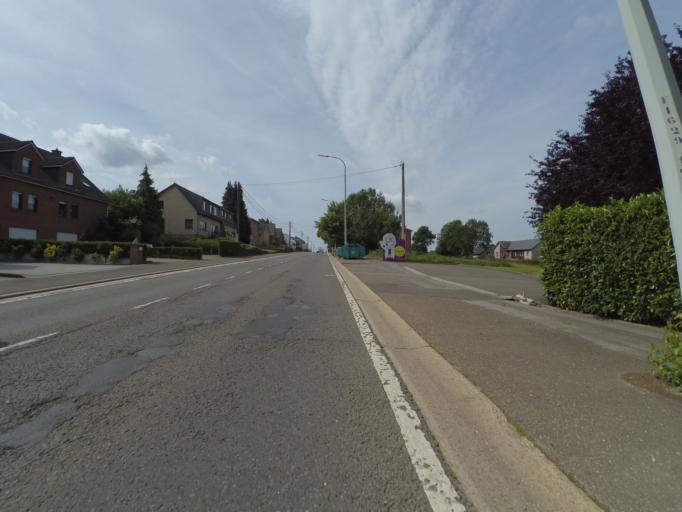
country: BE
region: Wallonia
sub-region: Province de Liege
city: Eupen
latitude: 50.6407
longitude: 6.0430
